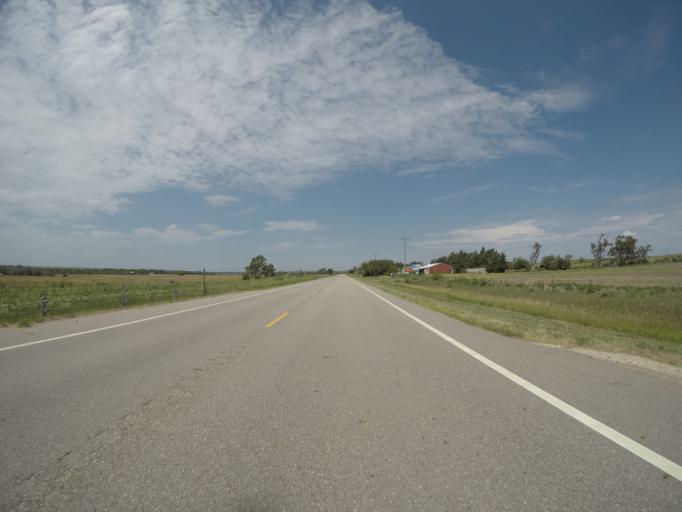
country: US
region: Kansas
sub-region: Rooks County
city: Stockton
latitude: 39.4443
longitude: -99.2204
